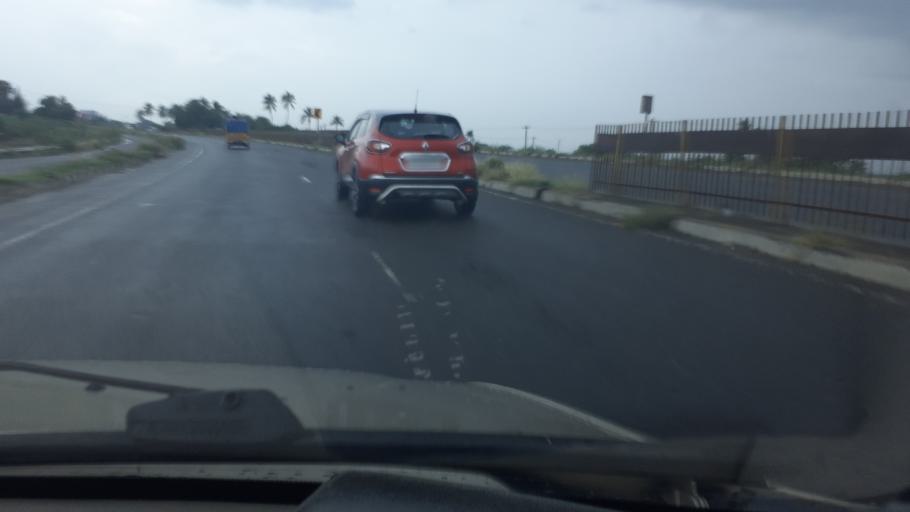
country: IN
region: Tamil Nadu
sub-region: Thoothukkudi
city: Kadambur
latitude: 9.0342
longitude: 77.7894
